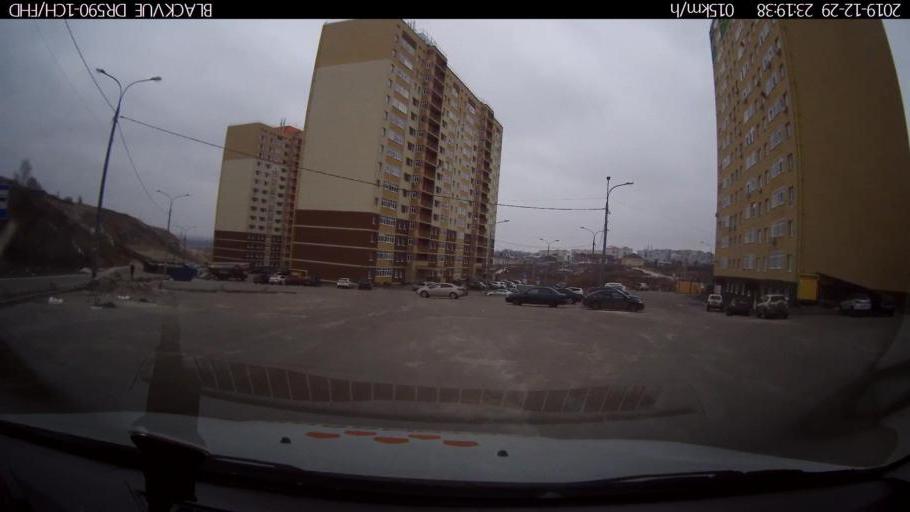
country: RU
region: Nizjnij Novgorod
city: Afonino
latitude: 56.2815
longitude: 44.0886
